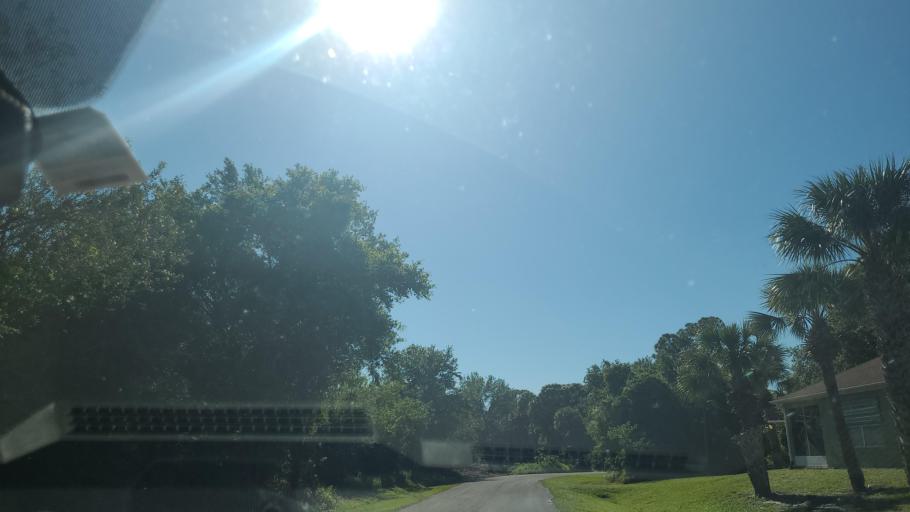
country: US
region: Florida
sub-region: Indian River County
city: Sebastian
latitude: 27.7561
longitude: -80.4857
